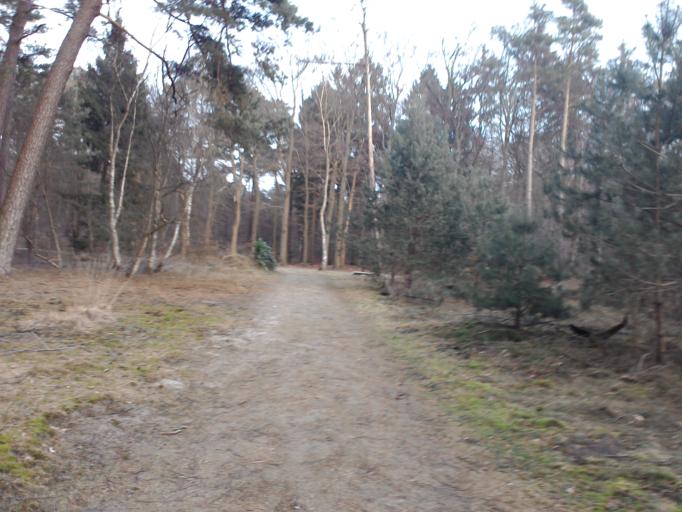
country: NL
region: Utrecht
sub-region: Gemeente Zeist
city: Zeist
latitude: 52.1096
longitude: 5.2127
